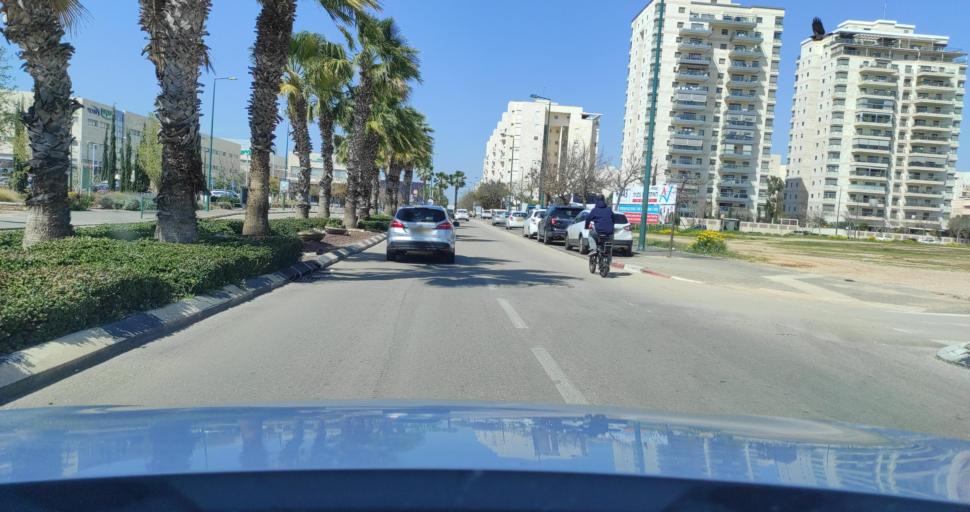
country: IL
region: Central District
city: Nordiyya
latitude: 32.3050
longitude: 34.8697
